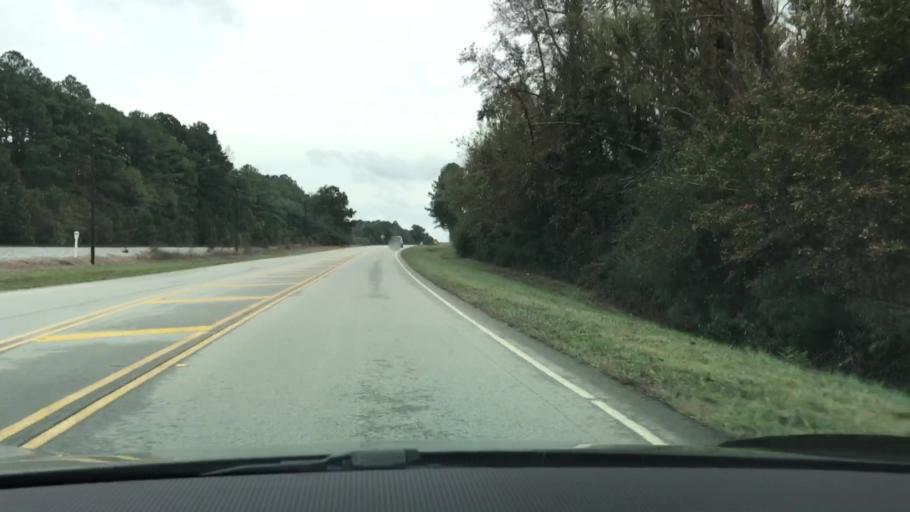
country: US
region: Georgia
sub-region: Warren County
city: Firing Range
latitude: 33.4770
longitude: -82.7320
